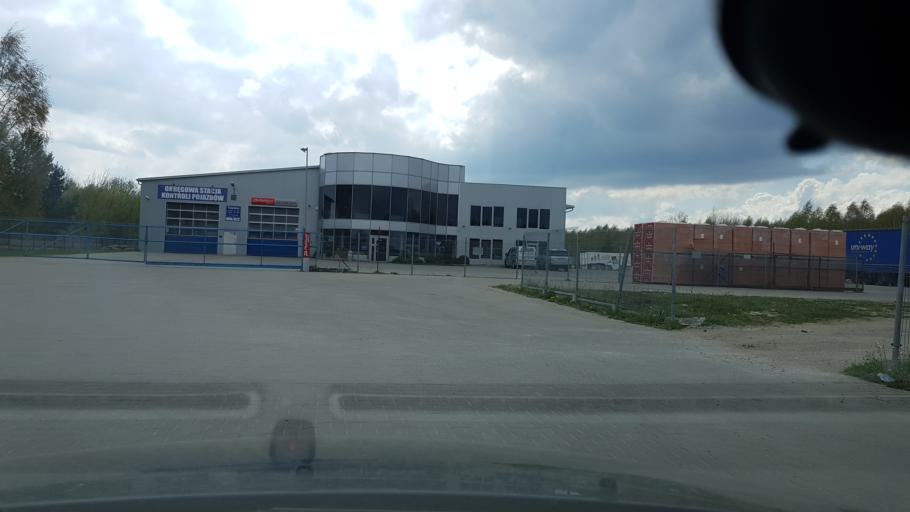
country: PL
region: Masovian Voivodeship
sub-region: Powiat minski
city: Debe Wielkie
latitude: 52.1989
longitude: 21.4970
